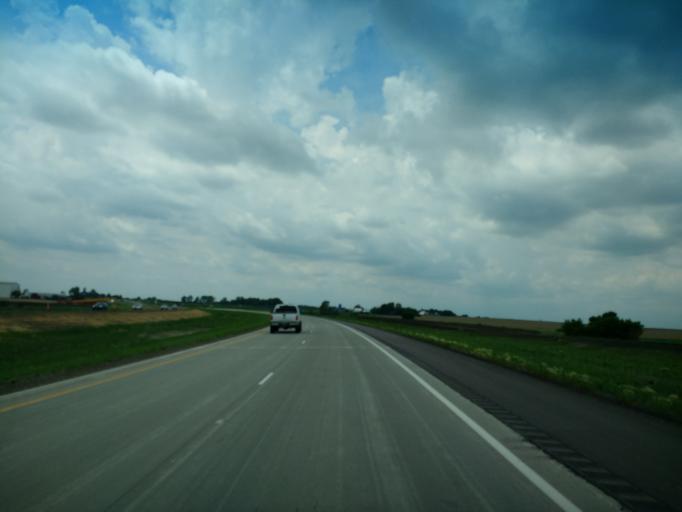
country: US
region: Minnesota
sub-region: Cottonwood County
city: Windom
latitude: 43.9097
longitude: -95.0518
